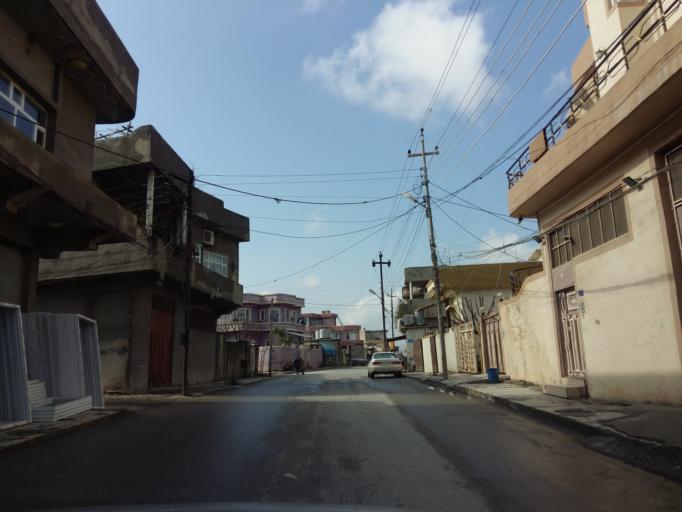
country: IQ
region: As Sulaymaniyah
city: Qeladize
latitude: 36.1863
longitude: 45.1204
